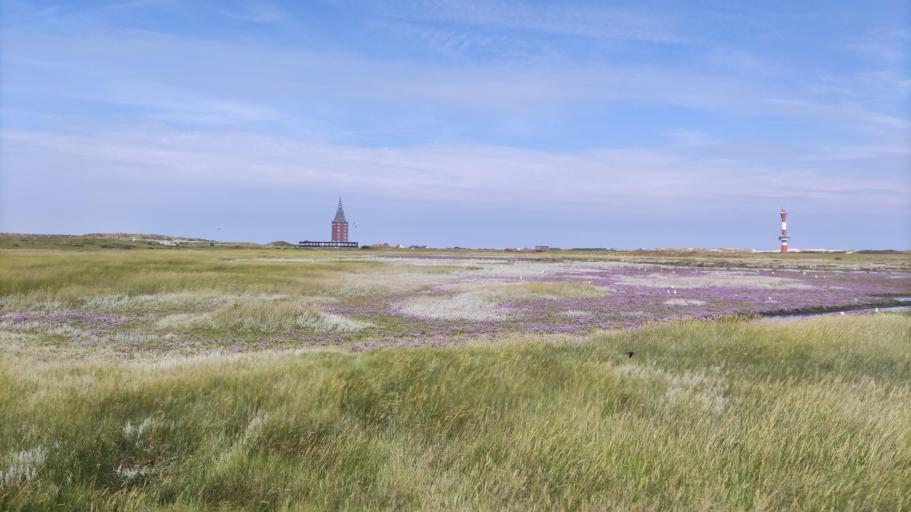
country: DE
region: Lower Saxony
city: Wangerooge
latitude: 53.7833
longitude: 7.8670
